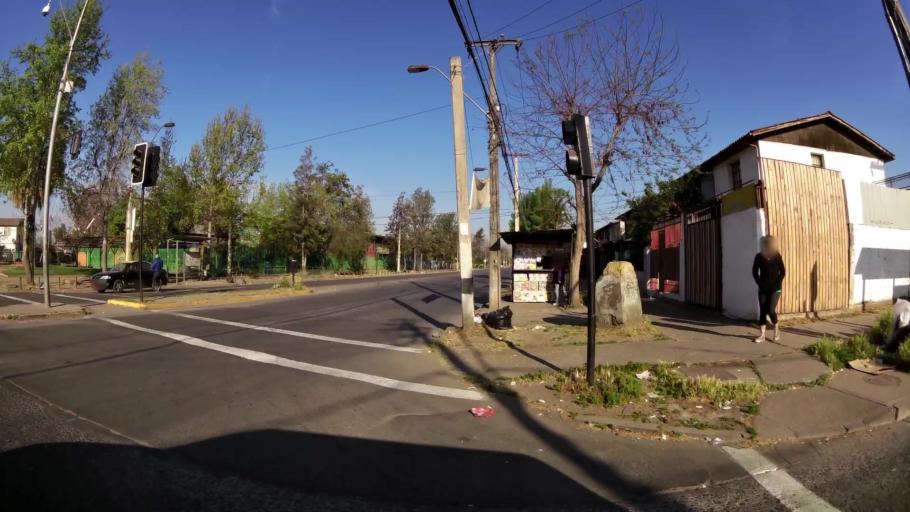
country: CL
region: Santiago Metropolitan
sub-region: Provincia de Santiago
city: Santiago
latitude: -33.3864
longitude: -70.6608
